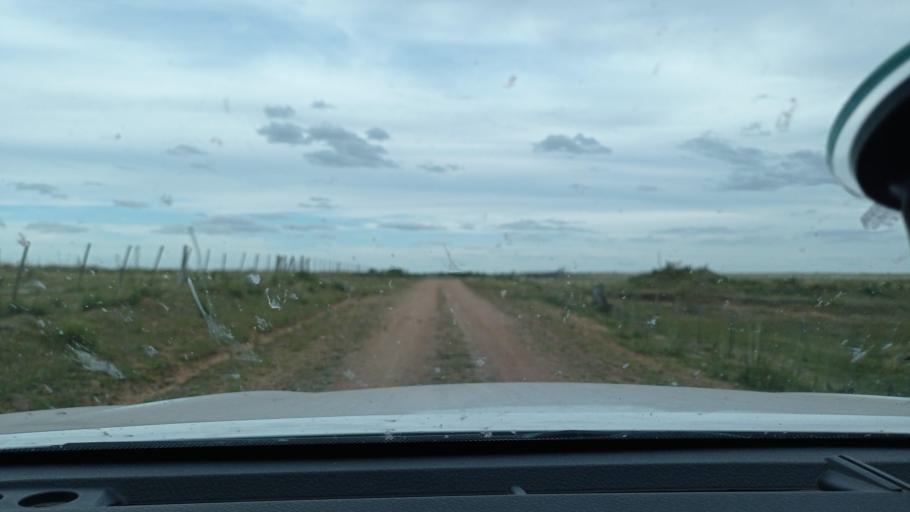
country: UY
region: Florida
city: Casupa
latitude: -34.1268
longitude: -55.8021
